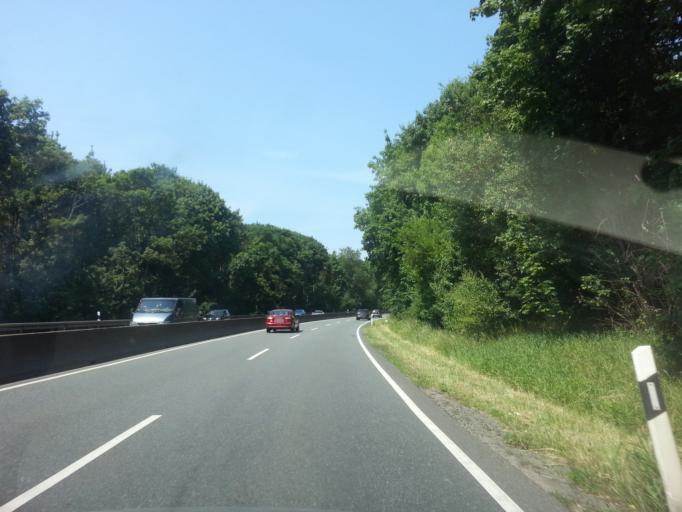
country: DE
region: Hesse
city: Pfungstadt
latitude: 49.8048
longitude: 8.6337
